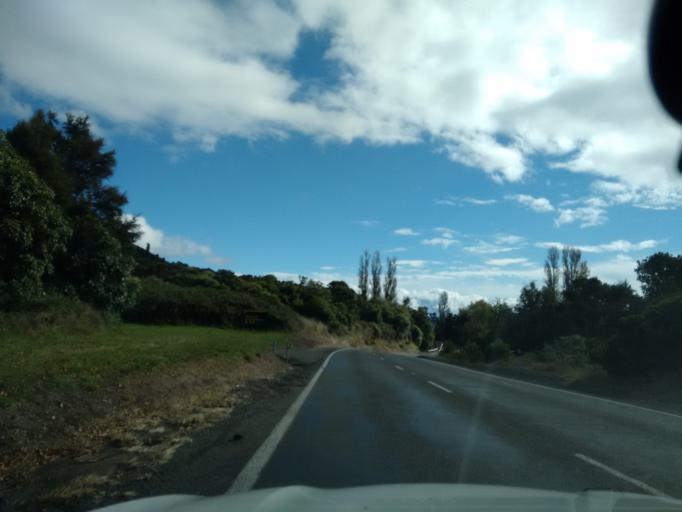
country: NZ
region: Waikato
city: Turangi
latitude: -38.8803
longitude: 175.9744
